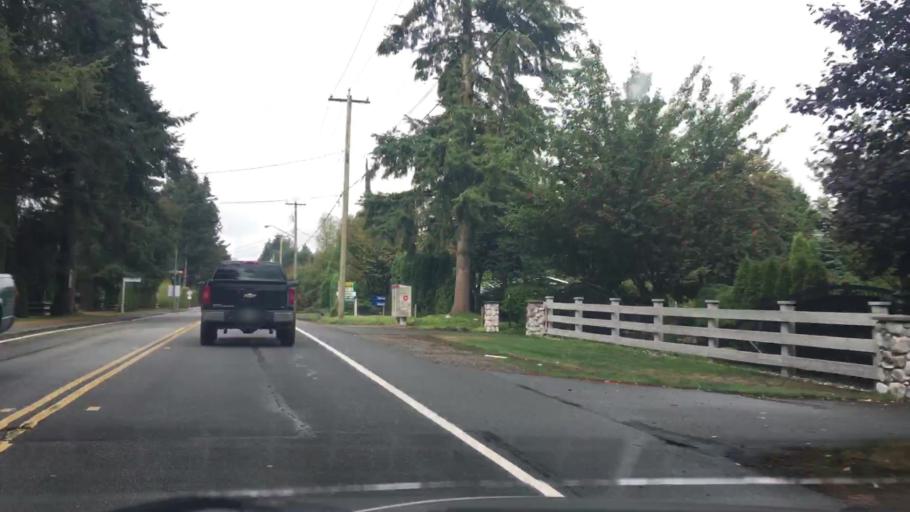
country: CA
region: British Columbia
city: Langley
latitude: 49.1042
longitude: -122.5544
